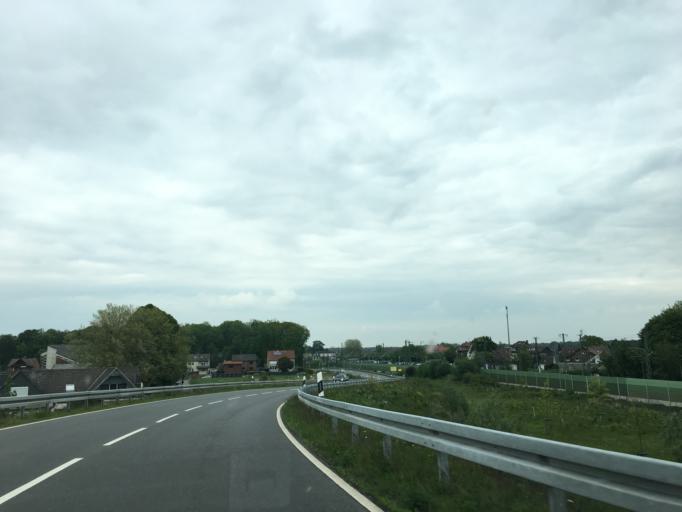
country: DE
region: Lower Saxony
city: Haste
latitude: 52.3756
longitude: 9.3821
